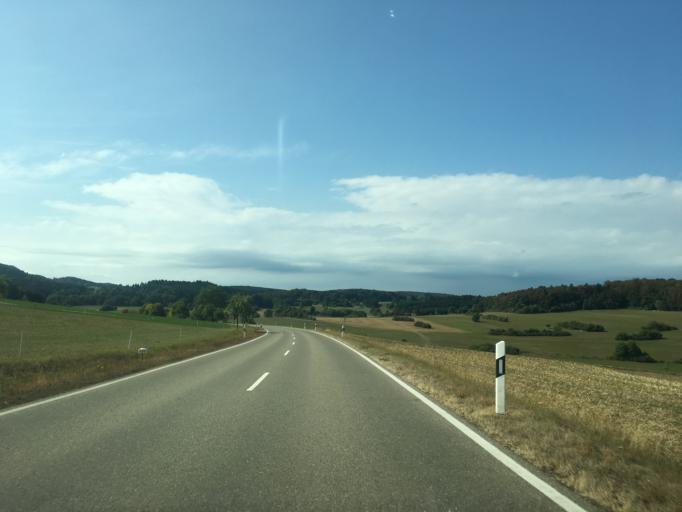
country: DE
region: Baden-Wuerttemberg
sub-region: Tuebingen Region
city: Trochtelfingen
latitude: 48.3661
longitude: 9.2144
